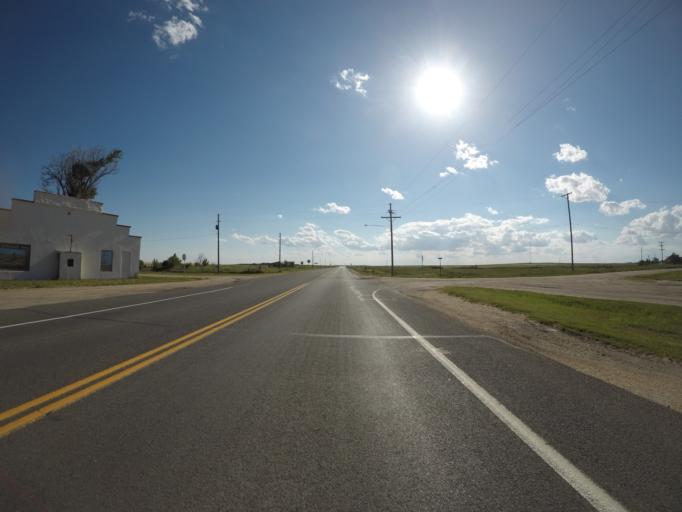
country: US
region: Colorado
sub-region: Morgan County
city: Fort Morgan
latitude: 40.6059
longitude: -103.8448
